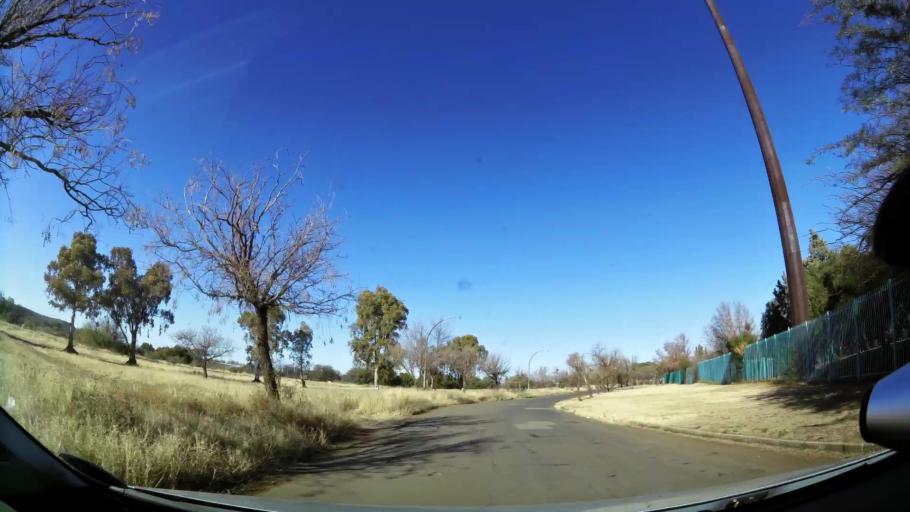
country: ZA
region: Northern Cape
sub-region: Frances Baard District Municipality
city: Kimberley
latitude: -28.7432
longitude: 24.7986
